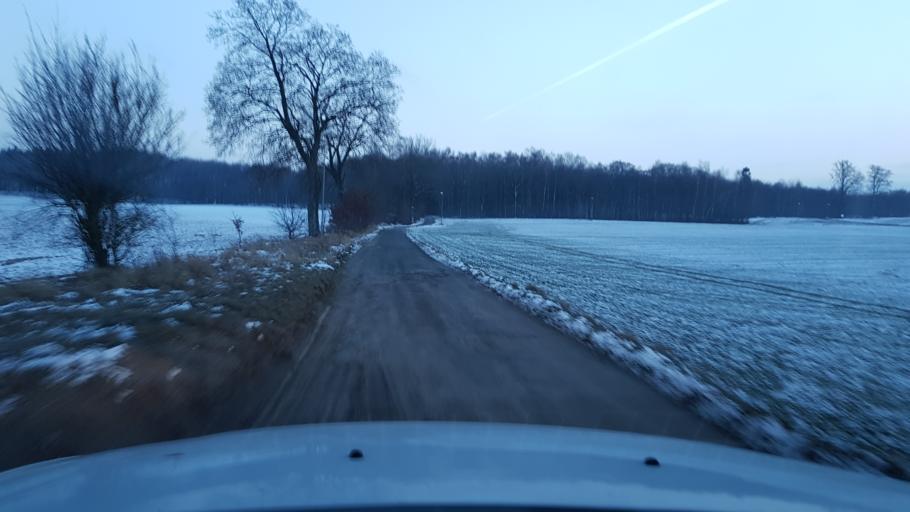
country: PL
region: West Pomeranian Voivodeship
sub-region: Powiat swidwinski
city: Slawoborze
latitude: 53.9669
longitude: 15.7652
